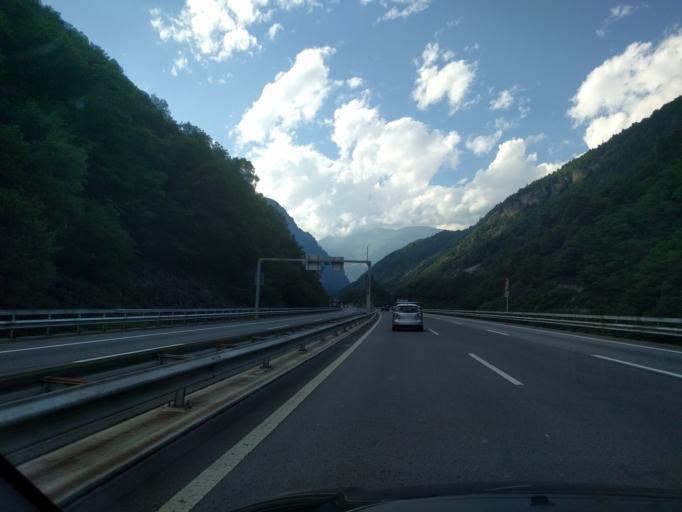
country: CH
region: Ticino
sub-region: Blenio District
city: Cancori
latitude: 46.4306
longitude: 8.8521
